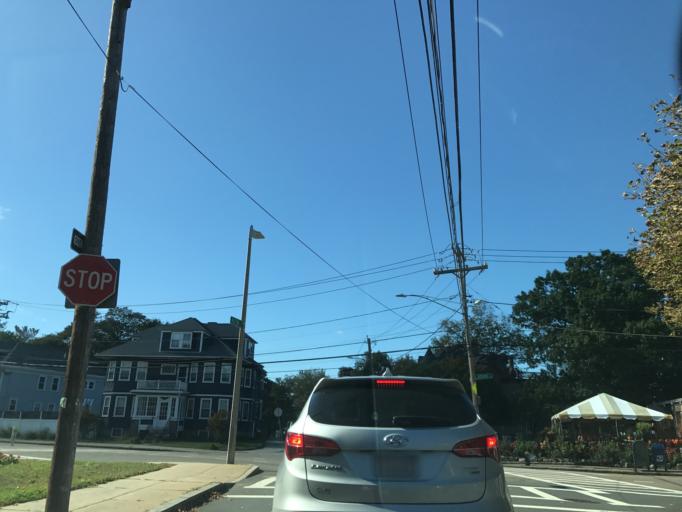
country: US
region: Massachusetts
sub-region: Norfolk County
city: Milton
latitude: 42.2801
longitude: -71.0584
